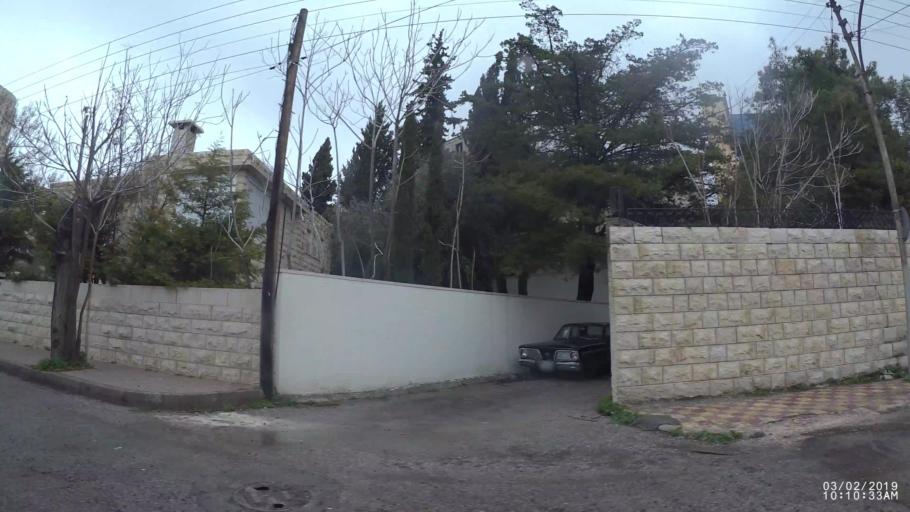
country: JO
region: Amman
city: Amman
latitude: 31.9524
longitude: 35.9118
